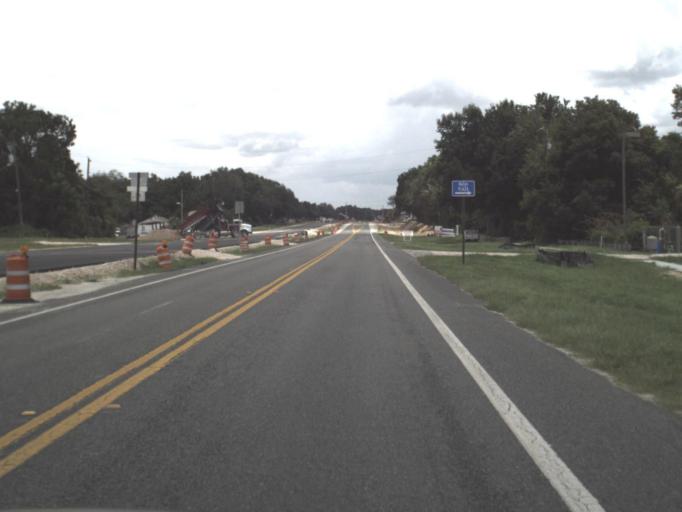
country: US
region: Florida
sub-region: Hillsborough County
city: Thonotosassa
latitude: 28.0488
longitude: -82.3394
